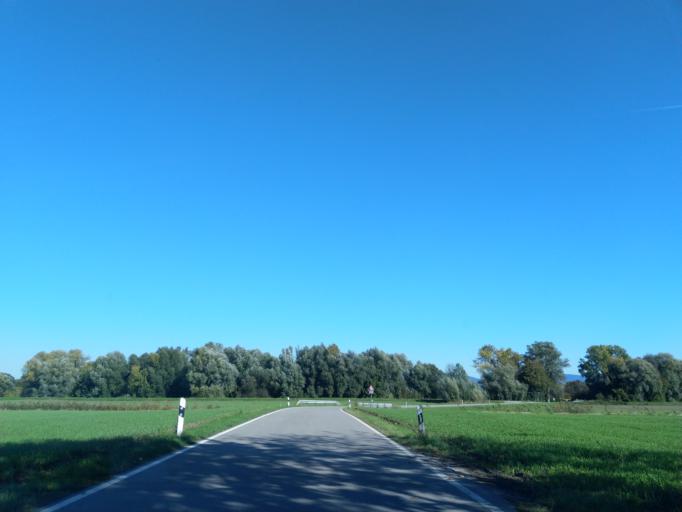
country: DE
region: Bavaria
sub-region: Lower Bavaria
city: Stephansposching
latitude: 48.8211
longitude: 12.8048
